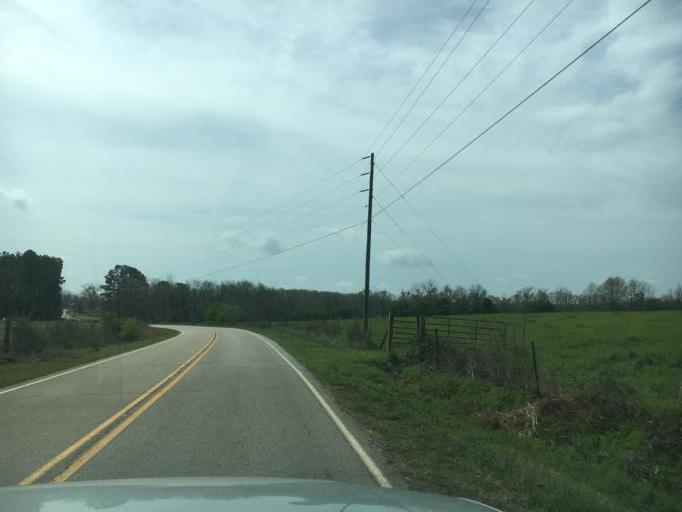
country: US
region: Georgia
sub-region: Hart County
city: Royston
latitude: 34.3467
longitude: -83.0413
